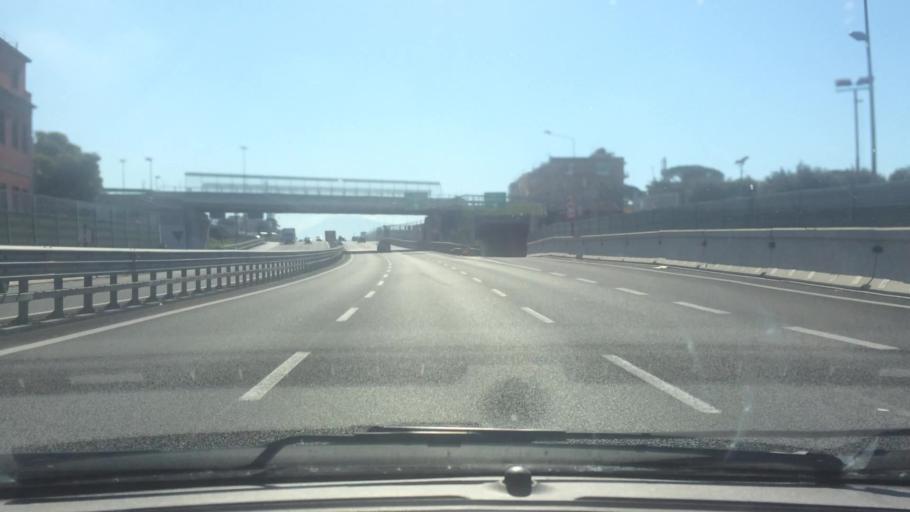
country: IT
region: Campania
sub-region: Provincia di Napoli
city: Ercolano
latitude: 40.8177
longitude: 14.3540
